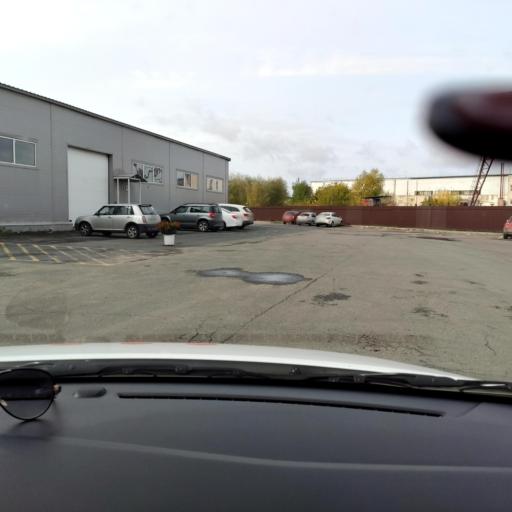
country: RU
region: Tatarstan
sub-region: Gorod Kazan'
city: Kazan
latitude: 55.7288
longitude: 49.1126
